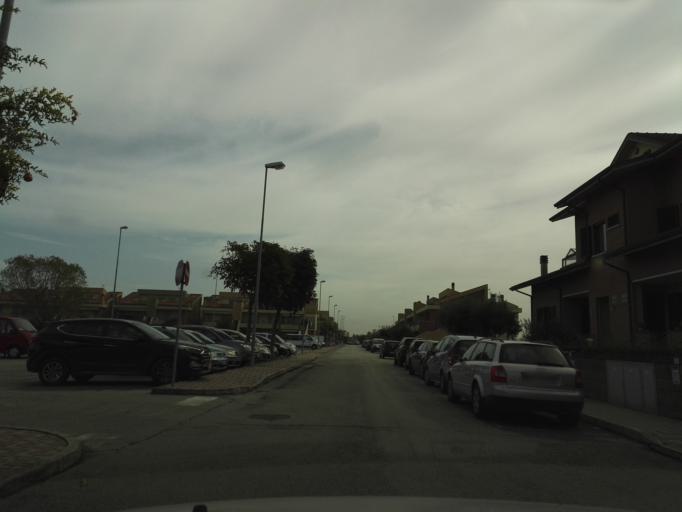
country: IT
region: The Marches
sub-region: Provincia di Pesaro e Urbino
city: Marotta
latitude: 43.7630
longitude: 13.1402
